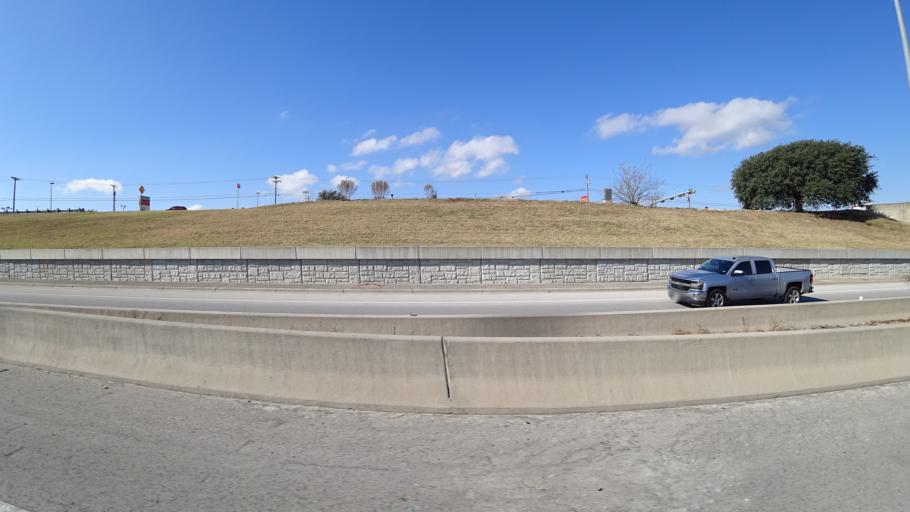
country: US
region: Texas
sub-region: Williamson County
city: Round Rock
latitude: 30.4883
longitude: -97.6768
